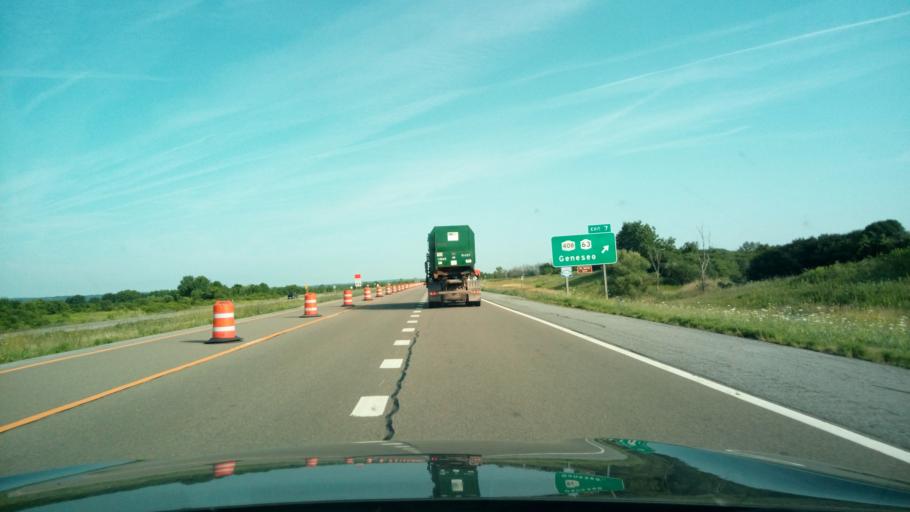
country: US
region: New York
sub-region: Livingston County
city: Mount Morris
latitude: 42.7313
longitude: -77.8334
